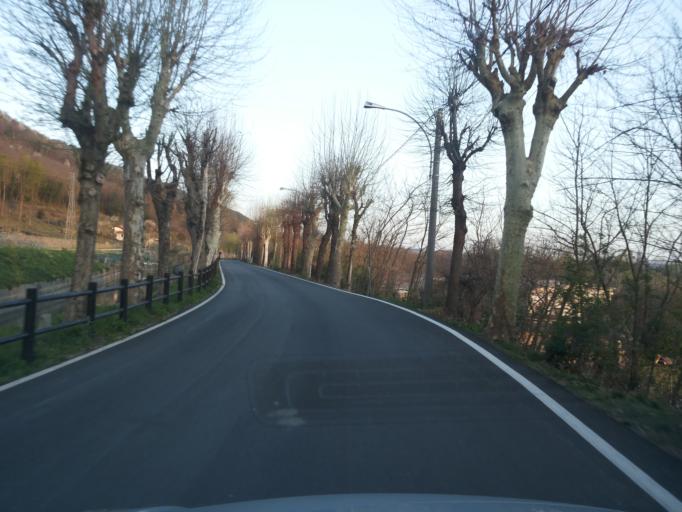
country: IT
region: Piedmont
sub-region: Provincia di Torino
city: Vestigne
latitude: 45.3846
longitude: 7.9584
